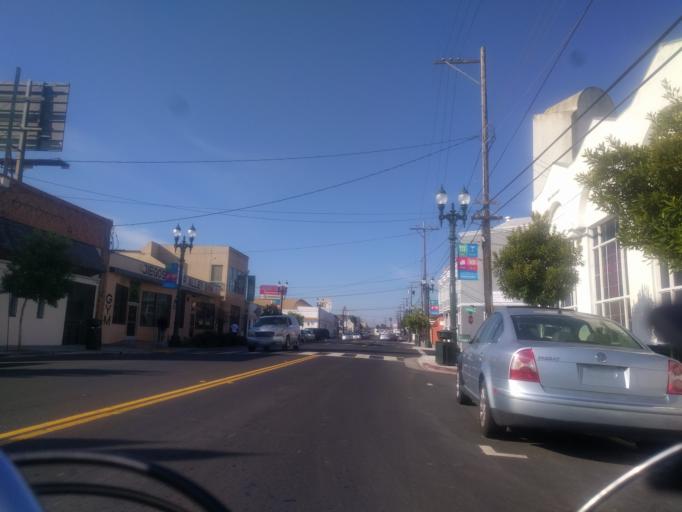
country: US
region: California
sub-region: Alameda County
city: Alameda
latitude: 37.7719
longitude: -122.1919
